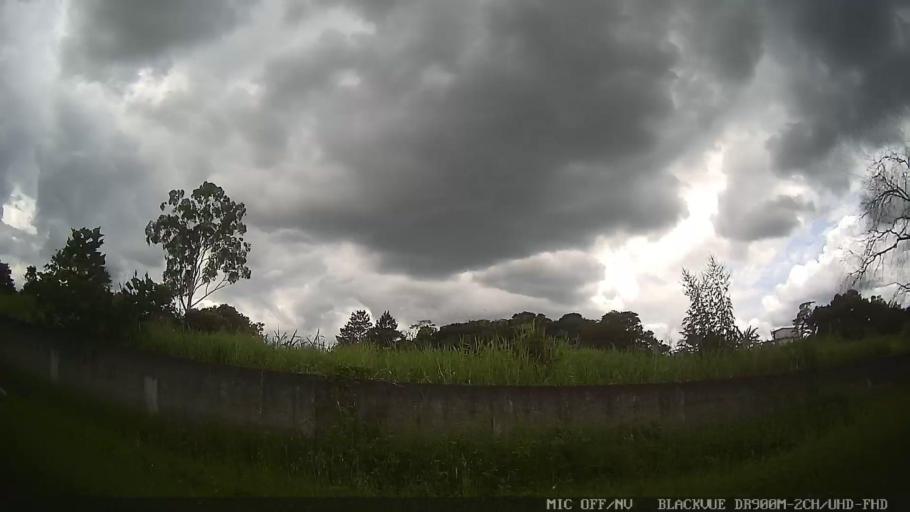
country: BR
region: Sao Paulo
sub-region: Suzano
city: Suzano
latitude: -23.6251
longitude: -46.3017
